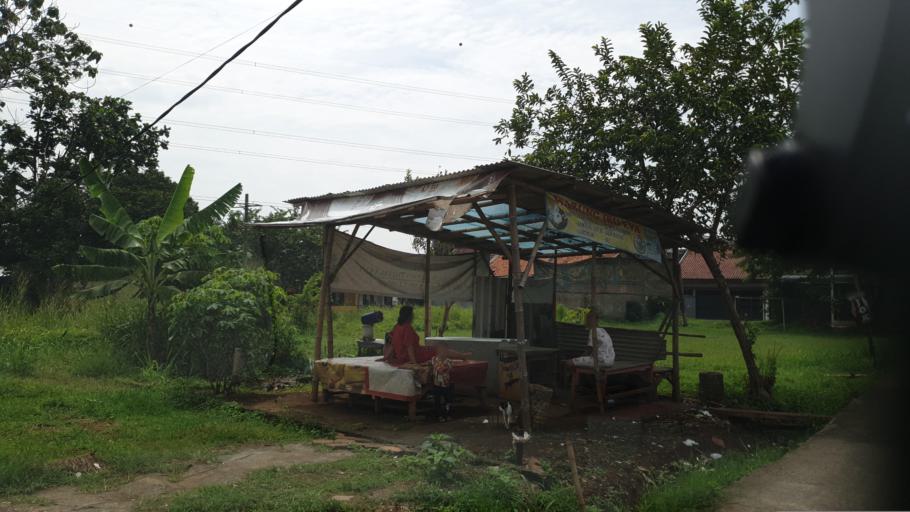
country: ID
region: West Java
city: Sawangan
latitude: -6.3745
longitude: 106.7606
